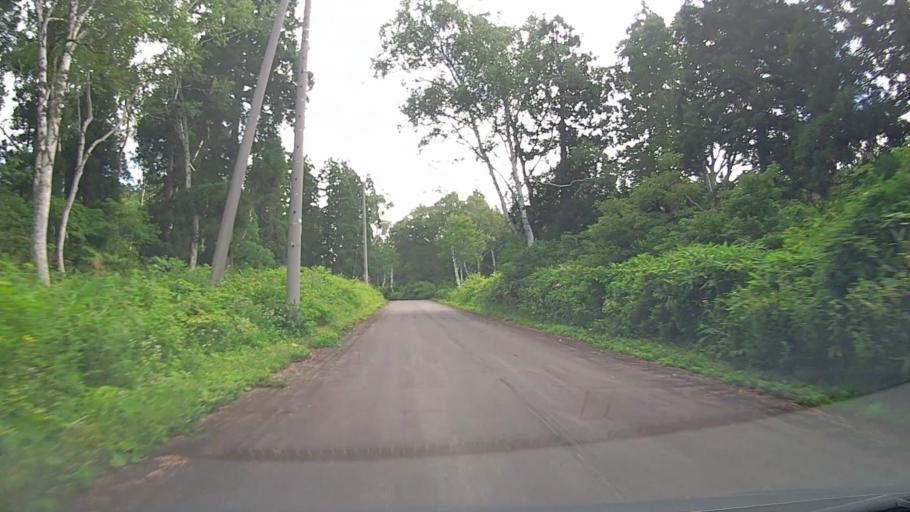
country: JP
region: Nagano
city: Iiyama
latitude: 36.9167
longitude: 138.4849
